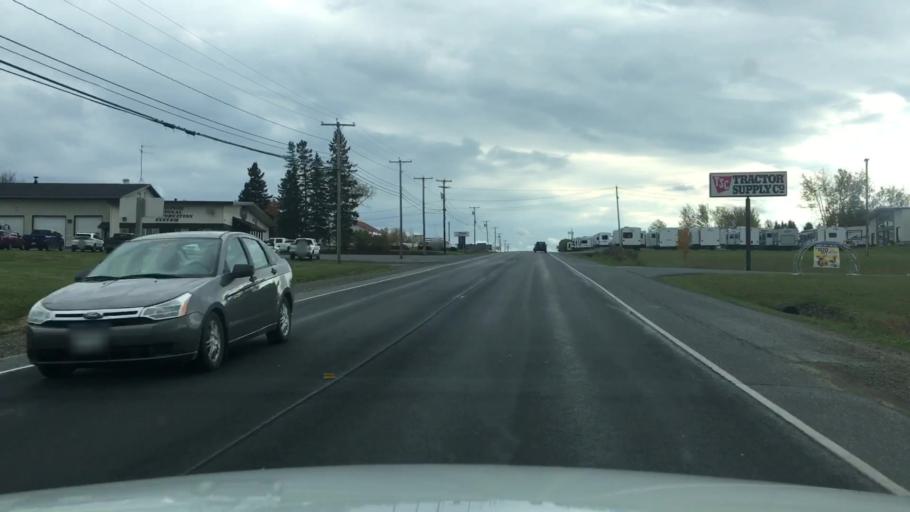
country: US
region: Maine
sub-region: Aroostook County
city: Presque Isle
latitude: 46.6615
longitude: -68.0085
